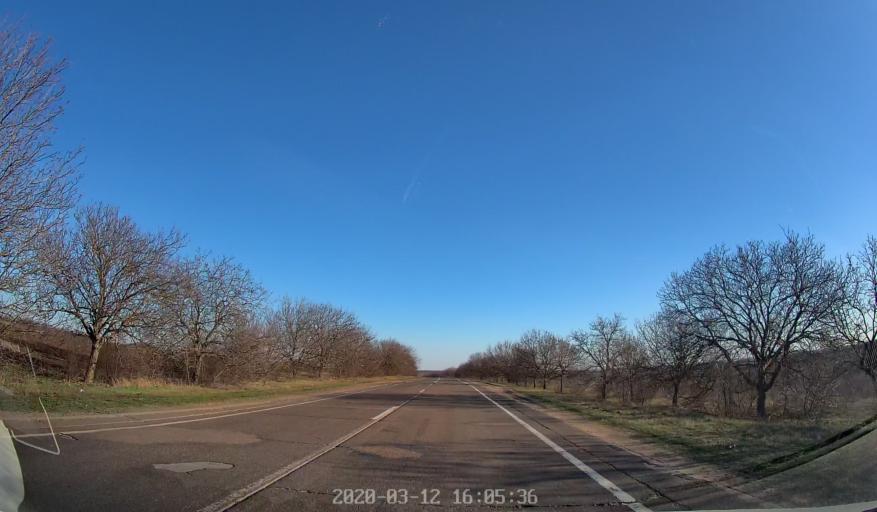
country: MD
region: Anenii Noi
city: Anenii Noi
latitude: 47.0024
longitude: 29.1806
